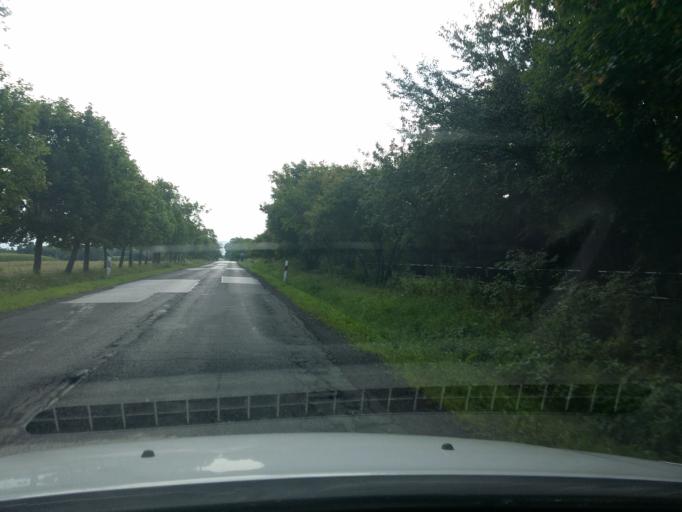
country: HU
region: Borsod-Abauj-Zemplen
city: Satoraljaujhely
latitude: 48.4719
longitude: 21.5479
